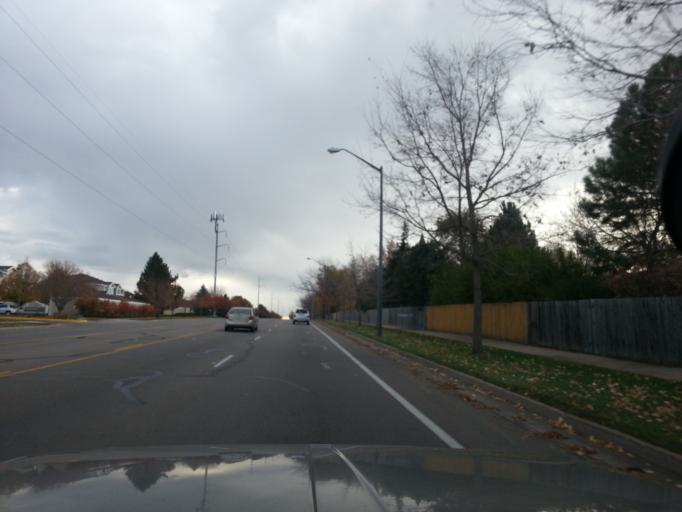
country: US
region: Colorado
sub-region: Larimer County
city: Fort Collins
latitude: 40.5527
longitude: -105.1033
